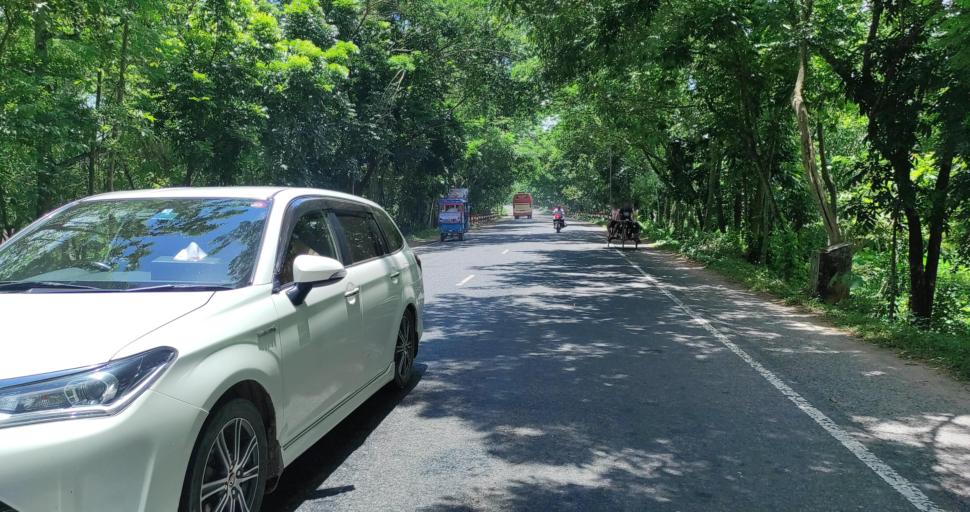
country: BD
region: Barisal
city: Gaurnadi
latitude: 22.8282
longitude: 90.2592
